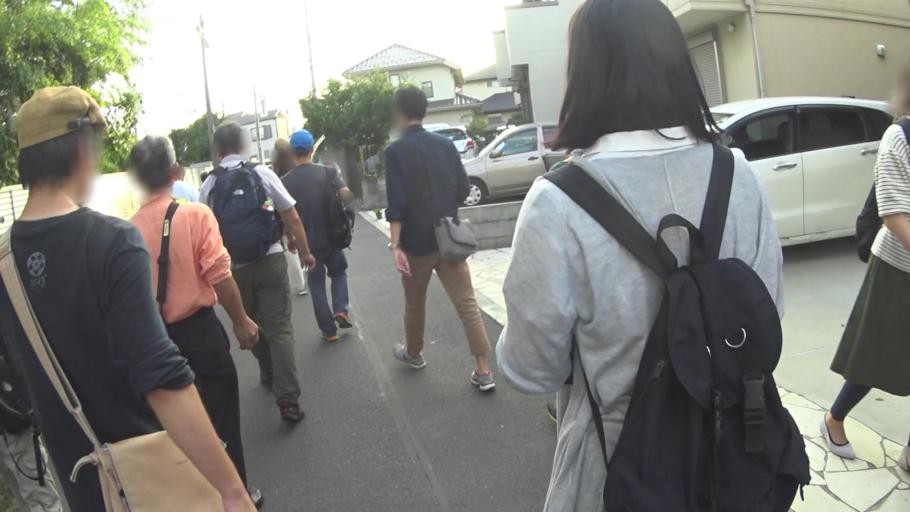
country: JP
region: Tokyo
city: Tanashicho
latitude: 35.7555
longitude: 139.5443
